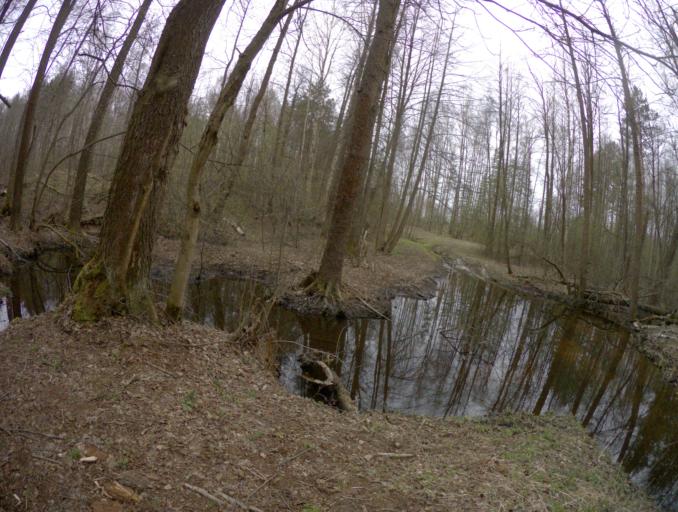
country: RU
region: Vladimir
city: Sudogda
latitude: 56.0382
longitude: 40.7930
